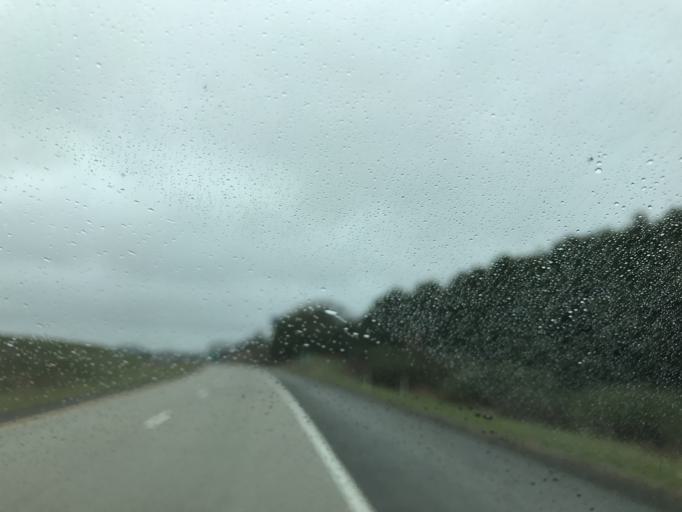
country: US
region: West Virginia
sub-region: Greenbrier County
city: Rainelle
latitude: 37.8460
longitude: -80.7296
